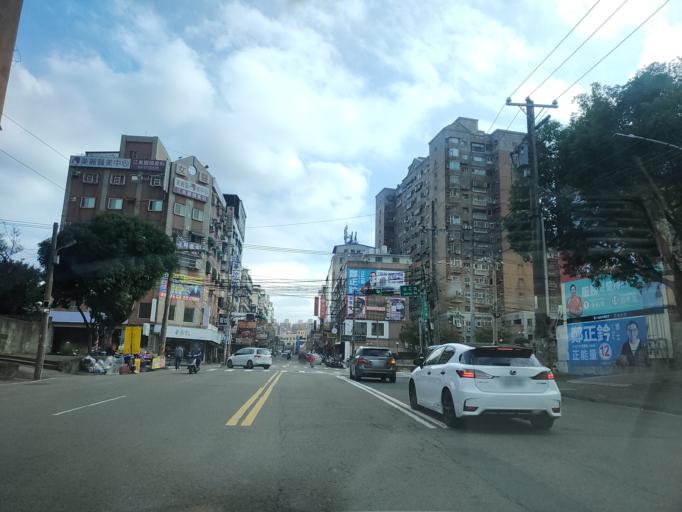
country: TW
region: Taiwan
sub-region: Hsinchu
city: Hsinchu
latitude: 24.7991
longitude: 120.9976
